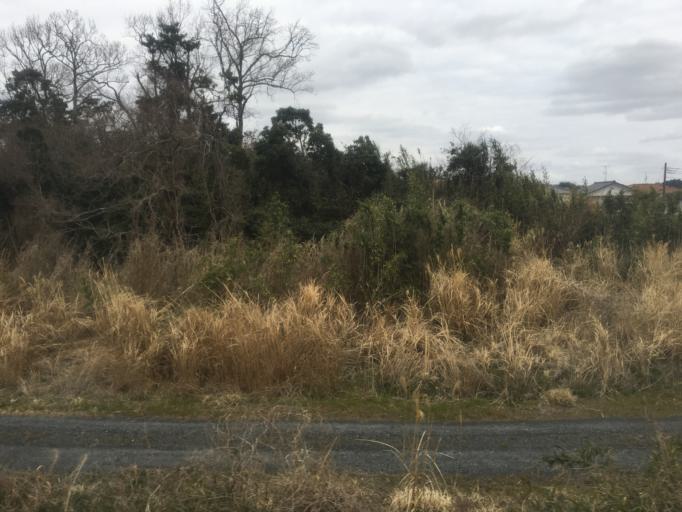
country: JP
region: Chiba
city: Oami
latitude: 35.5235
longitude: 140.3092
